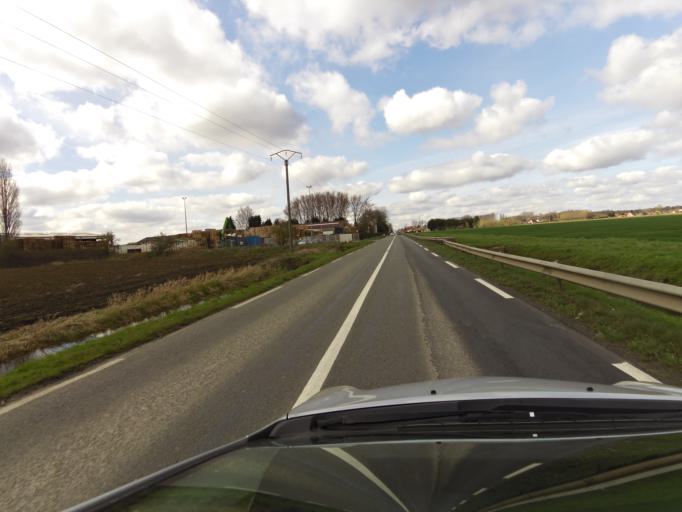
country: FR
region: Nord-Pas-de-Calais
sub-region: Departement du Pas-de-Calais
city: Lorgies
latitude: 50.5598
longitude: 2.7869
